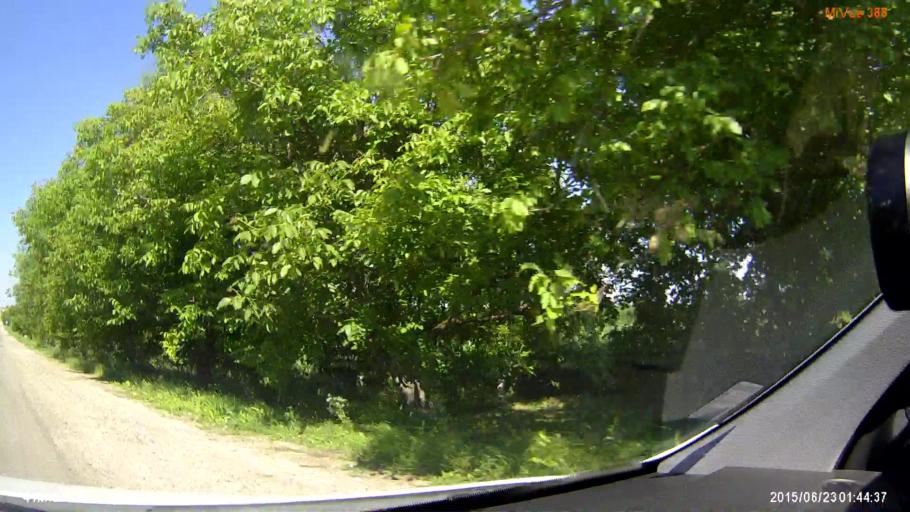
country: MD
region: Falesti
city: Falesti
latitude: 47.6236
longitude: 27.7498
